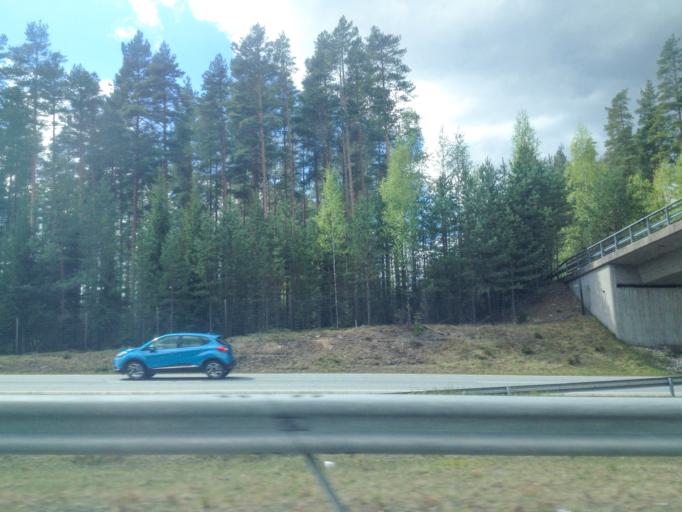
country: FI
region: Haeme
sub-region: Haemeenlinna
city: Janakkala
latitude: 60.9255
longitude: 24.5240
